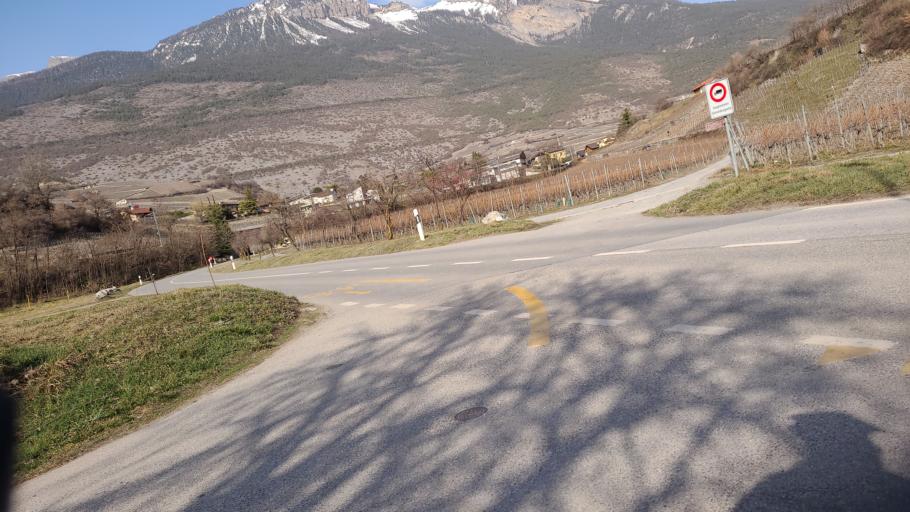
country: CH
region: Valais
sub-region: Leuk District
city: Salgesch
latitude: 46.3069
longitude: 7.5665
